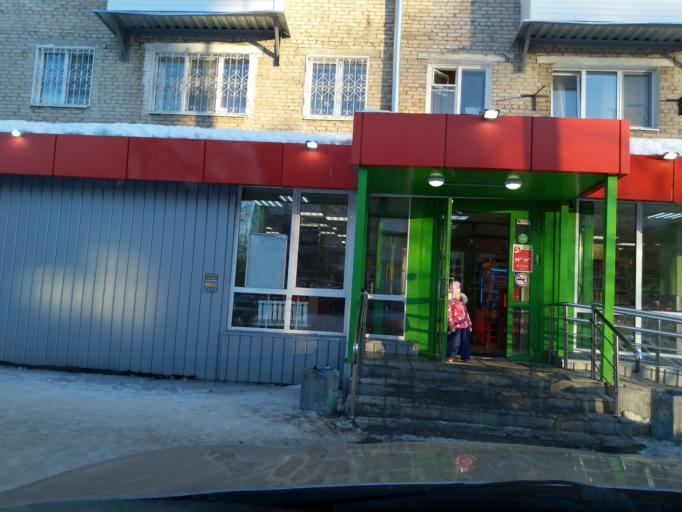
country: RU
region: Perm
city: Dobryanka
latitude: 58.4672
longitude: 56.3995
